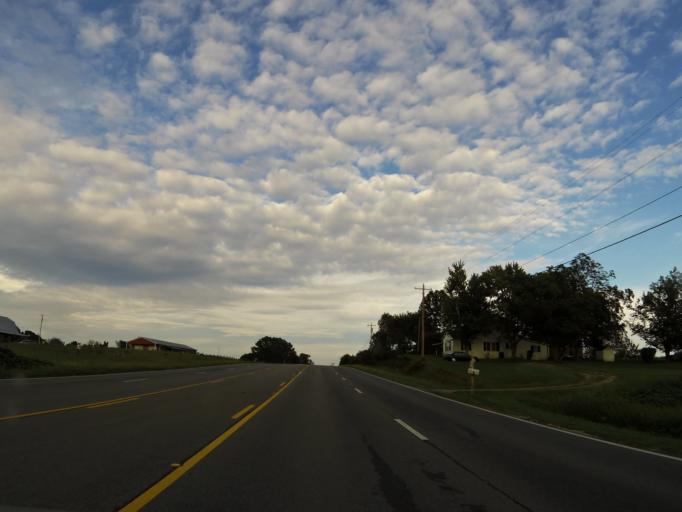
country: US
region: Alabama
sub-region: Lauderdale County
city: Rogersville
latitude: 34.8027
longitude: -87.2004
